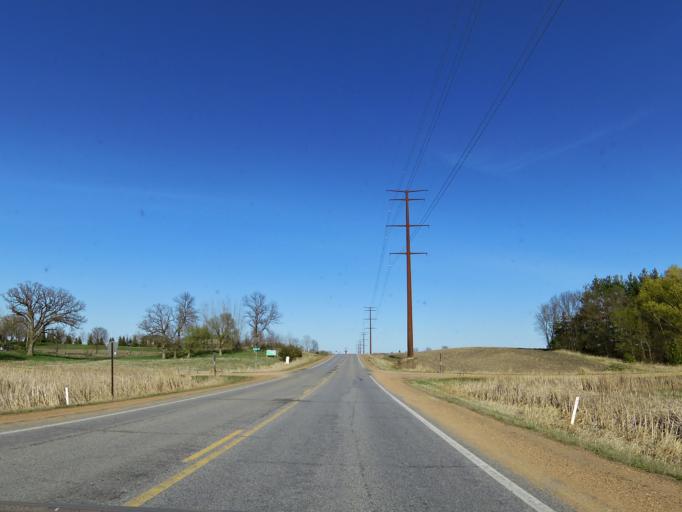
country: US
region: Minnesota
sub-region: Le Sueur County
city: New Prague
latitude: 44.5726
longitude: -93.4820
